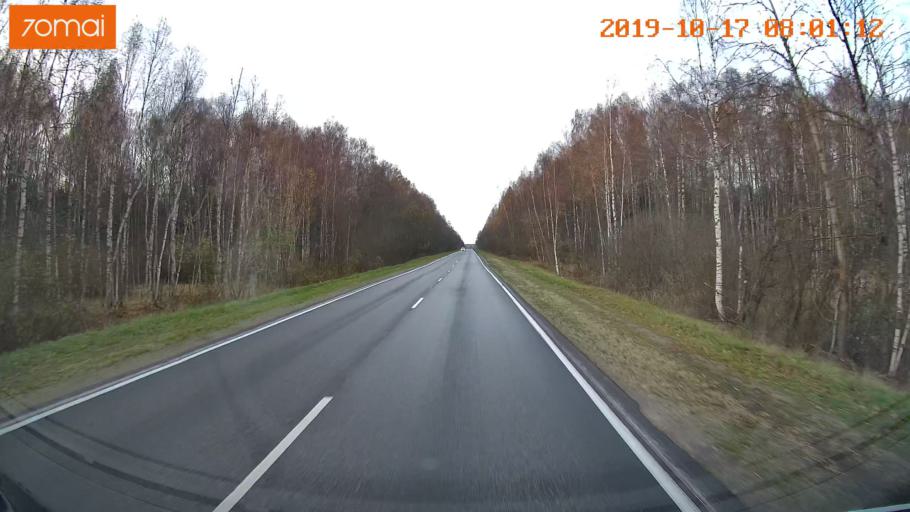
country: RU
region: Vladimir
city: Bavleny
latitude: 56.3754
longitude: 39.5016
